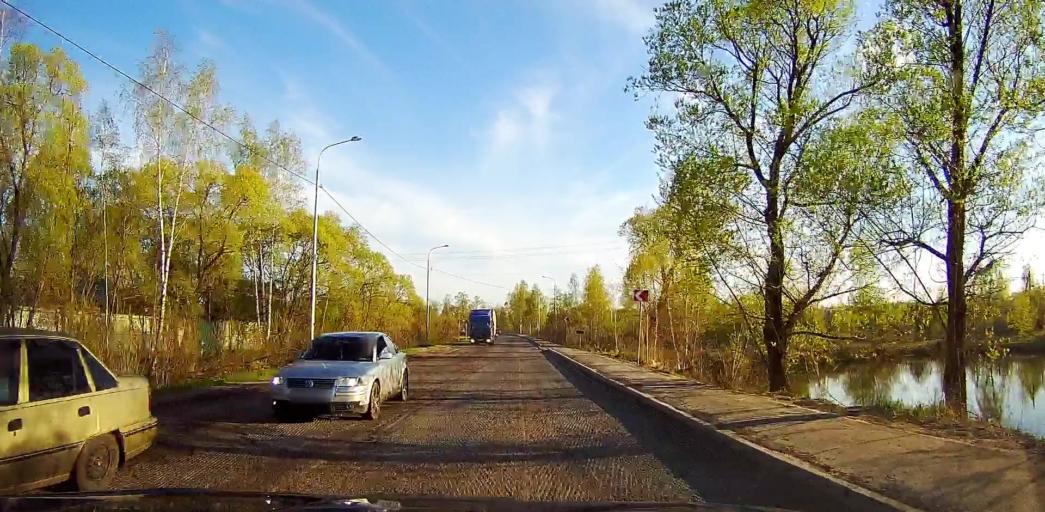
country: RU
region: Moskovskaya
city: Bronnitsy
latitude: 55.3034
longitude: 38.2108
